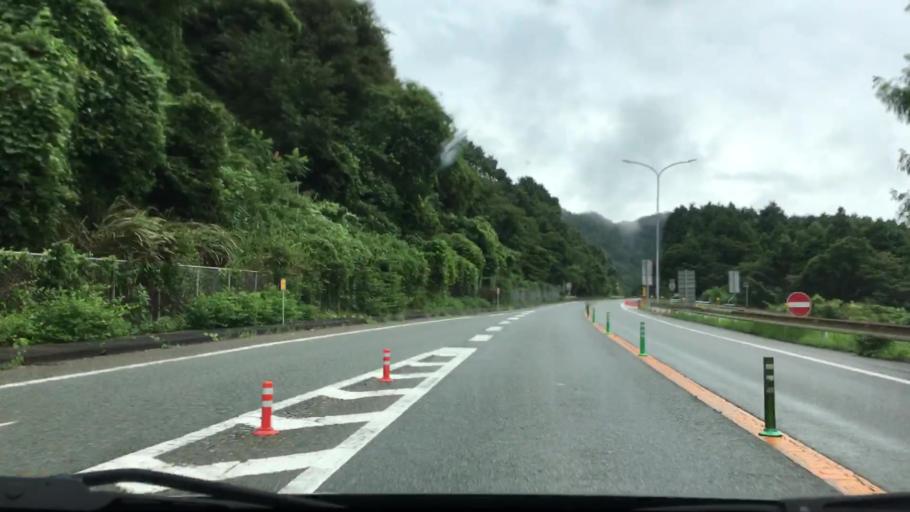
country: JP
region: Hyogo
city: Nishiwaki
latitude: 35.0238
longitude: 134.7664
